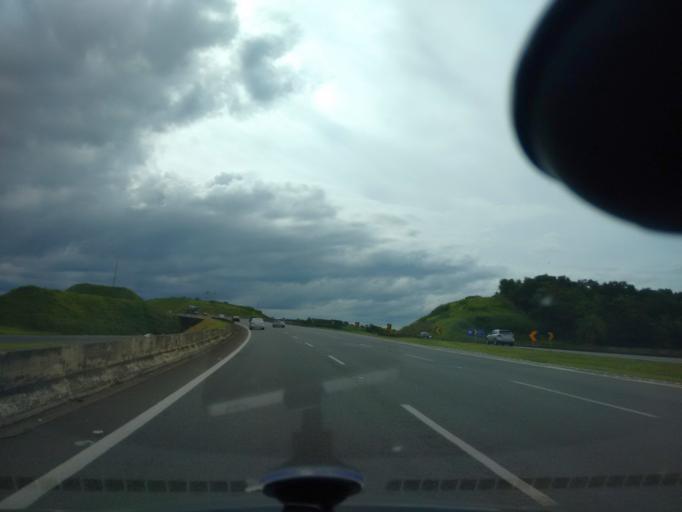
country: BR
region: Sao Paulo
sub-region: Campinas
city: Campinas
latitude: -22.9229
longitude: -47.1316
